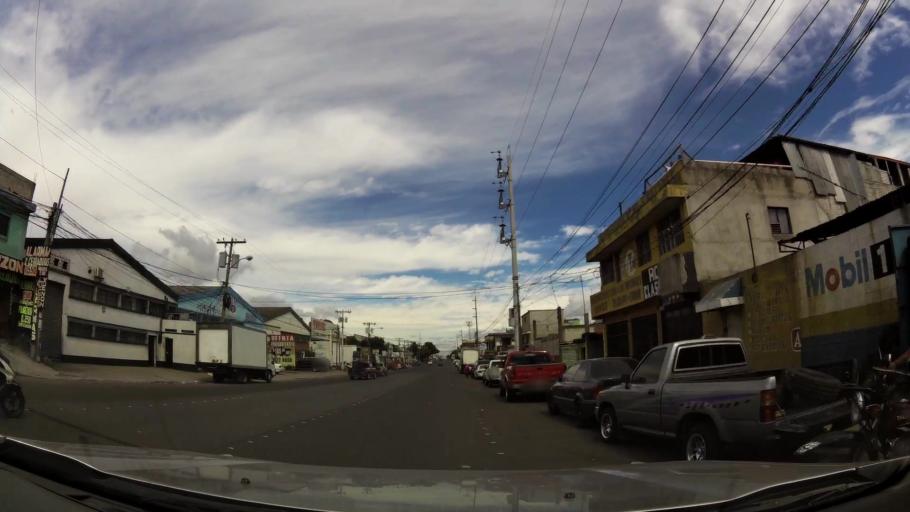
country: GT
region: Guatemala
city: Mixco
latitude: 14.6376
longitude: -90.5838
